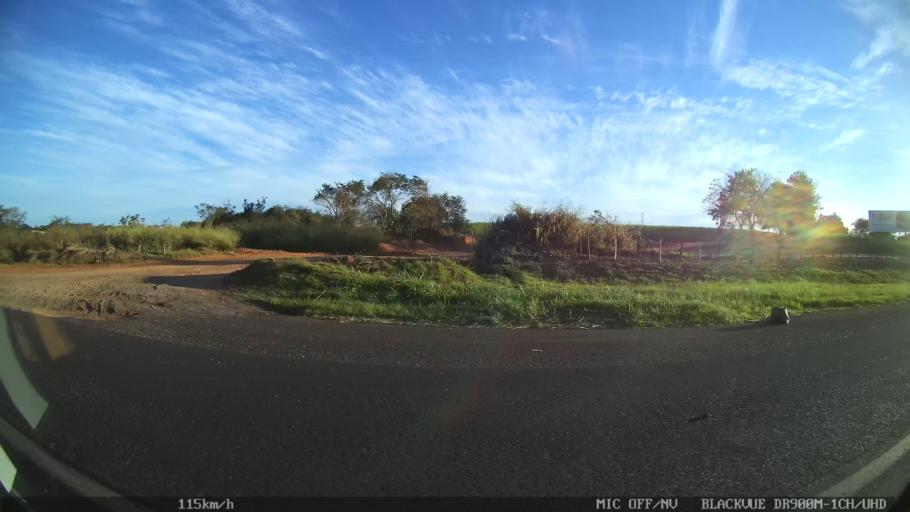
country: BR
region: Sao Paulo
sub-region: Catanduva
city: Catanduva
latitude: -21.0284
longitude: -49.1570
